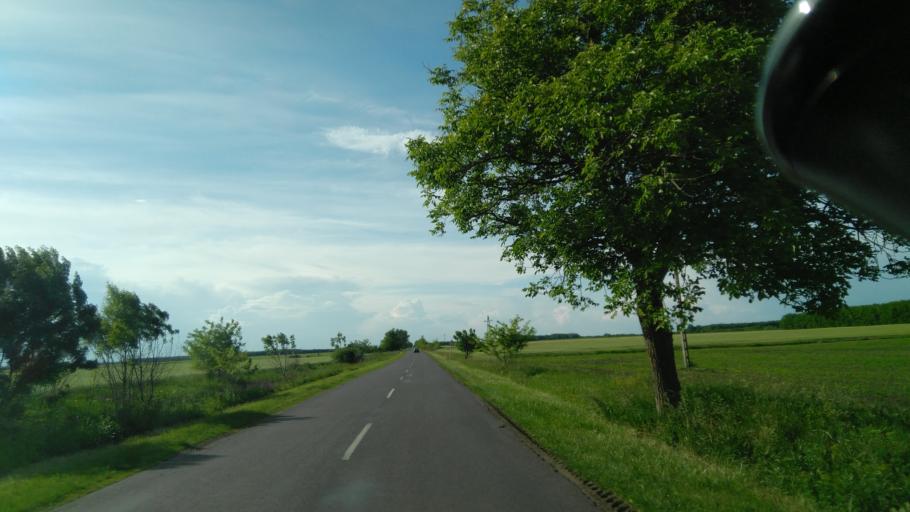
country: HU
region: Bekes
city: Lokoshaza
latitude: 46.4432
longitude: 21.2227
